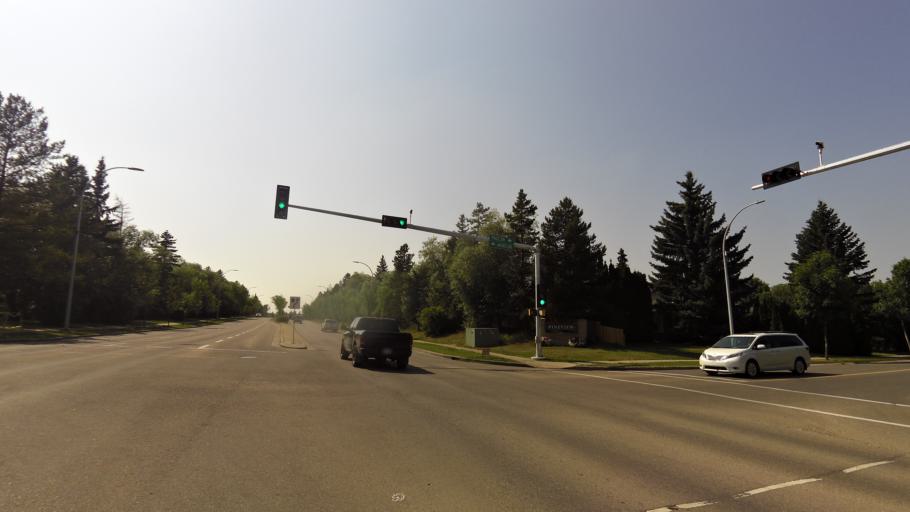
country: CA
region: Alberta
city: St. Albert
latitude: 53.6361
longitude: -113.5836
